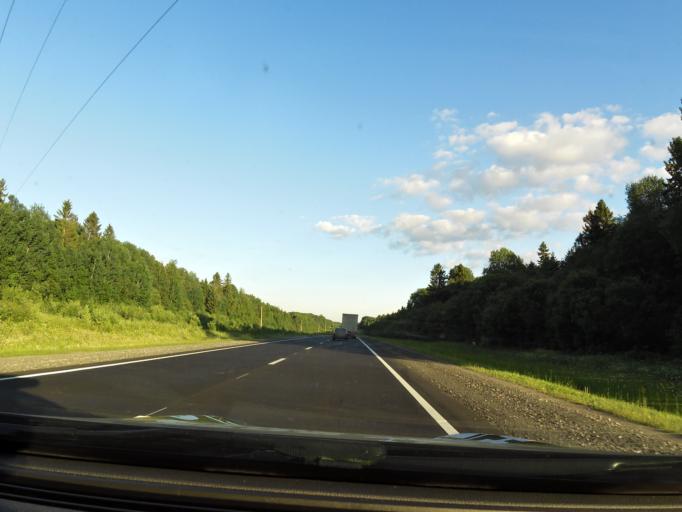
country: RU
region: Vologda
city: Gryazovets
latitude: 58.9966
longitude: 40.1317
